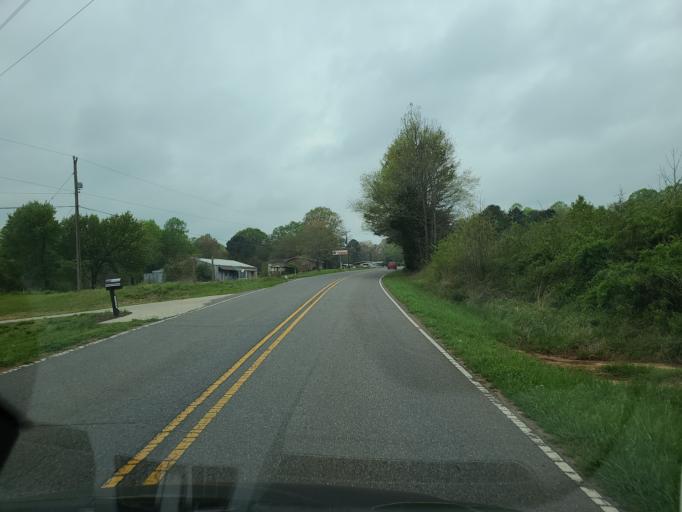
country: US
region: North Carolina
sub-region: Gaston County
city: Cherryville
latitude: 35.4272
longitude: -81.4808
